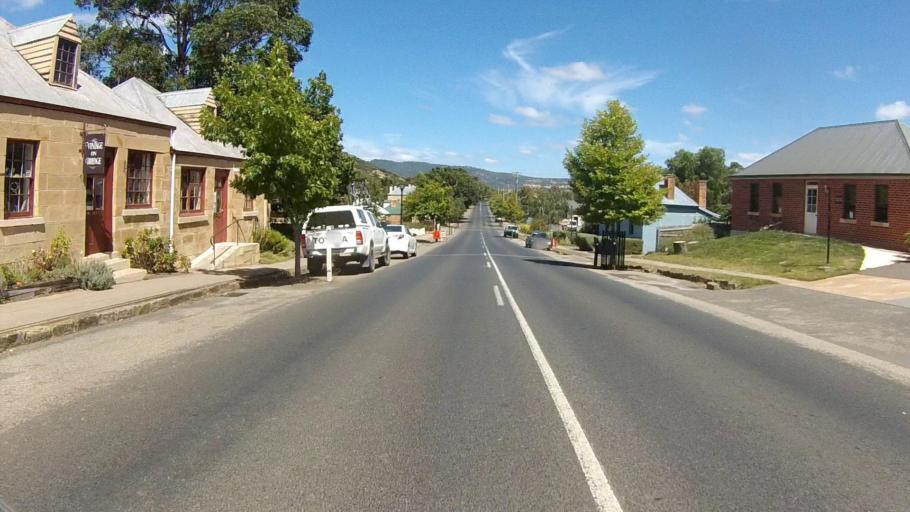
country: AU
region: Tasmania
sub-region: Clarence
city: Cambridge
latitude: -42.7368
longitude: 147.4351
